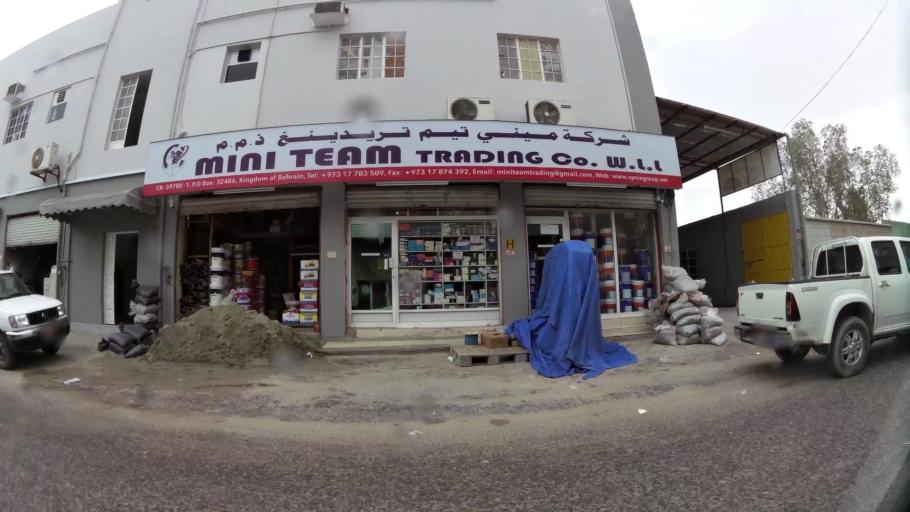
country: BH
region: Northern
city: Madinat `Isa
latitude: 26.1844
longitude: 50.5272
